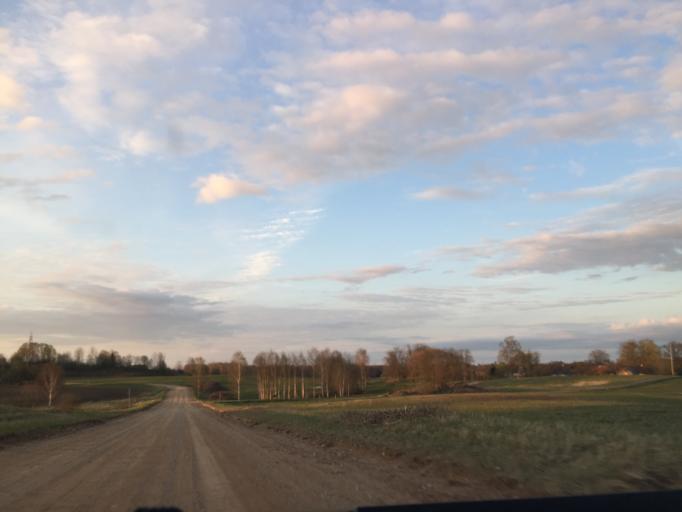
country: LV
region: Gulbenes Rajons
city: Gulbene
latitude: 57.2159
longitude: 26.7858
